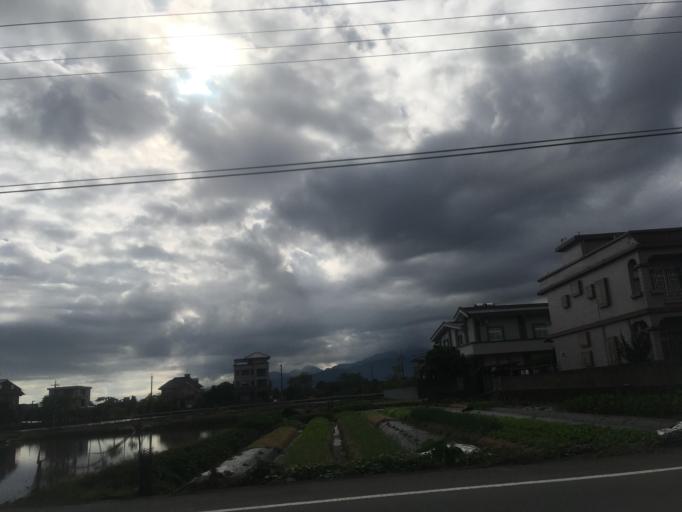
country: TW
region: Taiwan
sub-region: Yilan
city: Yilan
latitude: 24.6902
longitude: 121.7246
